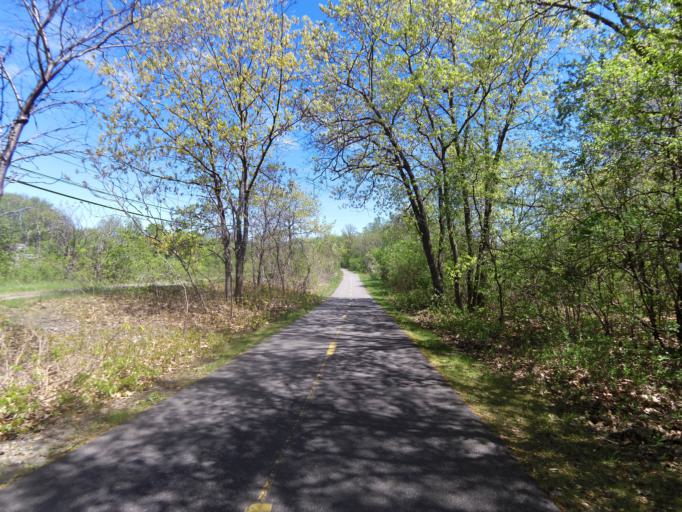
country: CA
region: Ontario
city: Bells Corners
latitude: 45.3843
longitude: -75.8212
